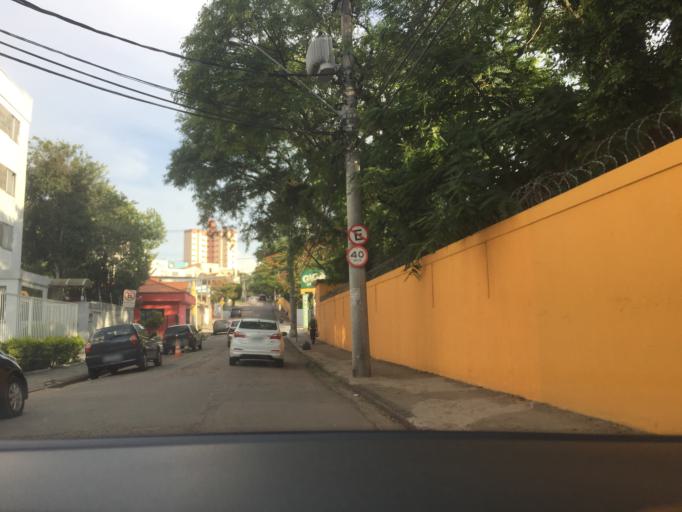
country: BR
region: Sao Paulo
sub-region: Jundiai
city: Jundiai
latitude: -23.2014
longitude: -46.8796
